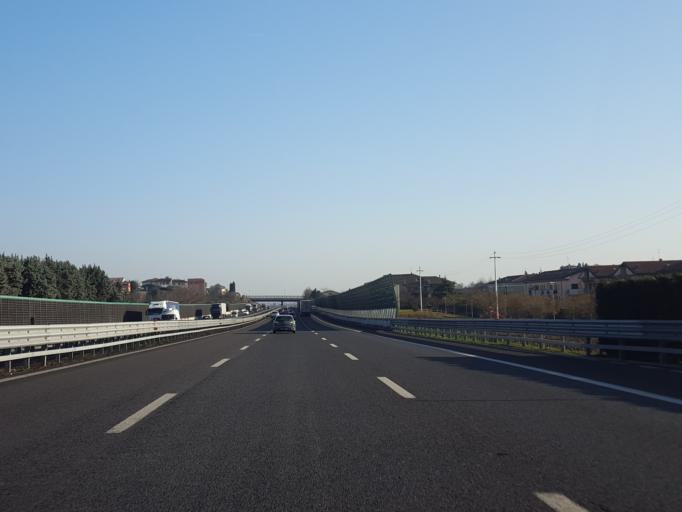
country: IT
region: Veneto
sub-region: Provincia di Verona
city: Caldiero
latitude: 45.4185
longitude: 11.1787
